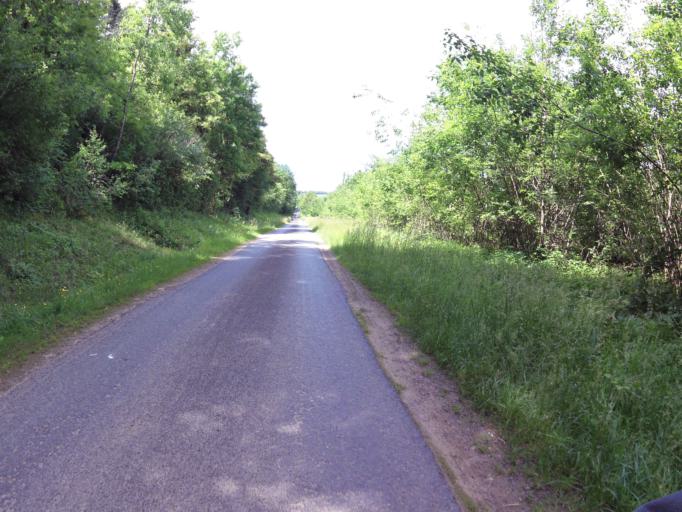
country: FR
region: Champagne-Ardenne
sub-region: Departement des Ardennes
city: Mouzon
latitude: 49.5385
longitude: 5.0863
